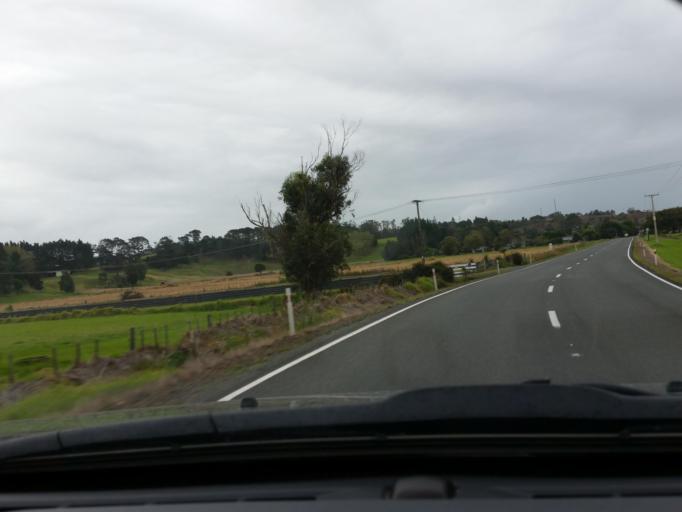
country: NZ
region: Northland
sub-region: Kaipara District
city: Dargaville
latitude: -35.9699
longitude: 173.8725
